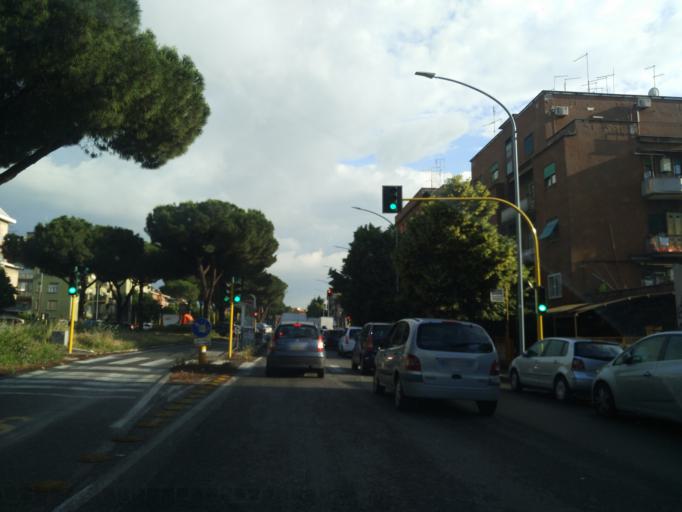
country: IT
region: Latium
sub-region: Citta metropolitana di Roma Capitale
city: Rome
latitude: 41.8817
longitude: 12.5730
